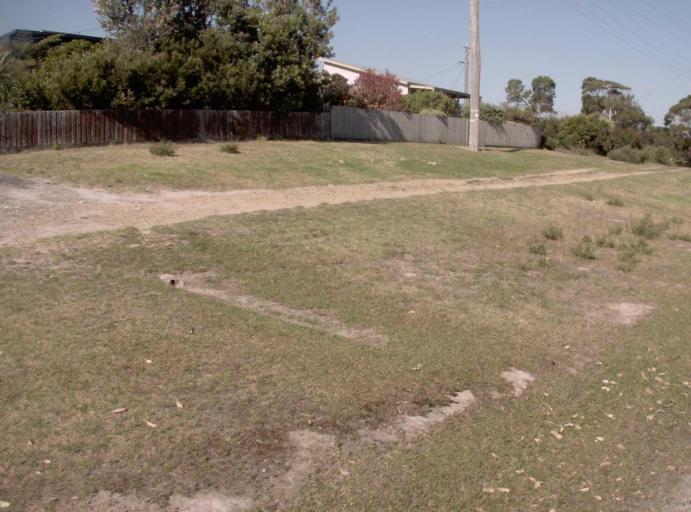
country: AU
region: Victoria
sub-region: East Gippsland
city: Lakes Entrance
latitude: -37.7973
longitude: 148.5400
